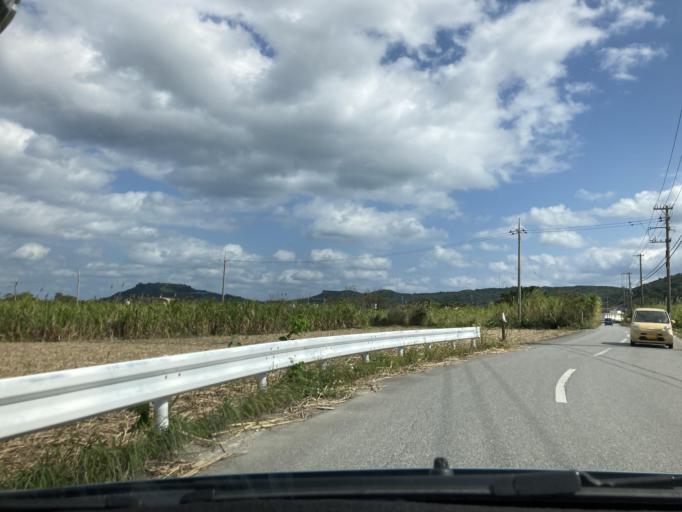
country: JP
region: Okinawa
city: Ginowan
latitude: 26.1691
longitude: 127.7784
